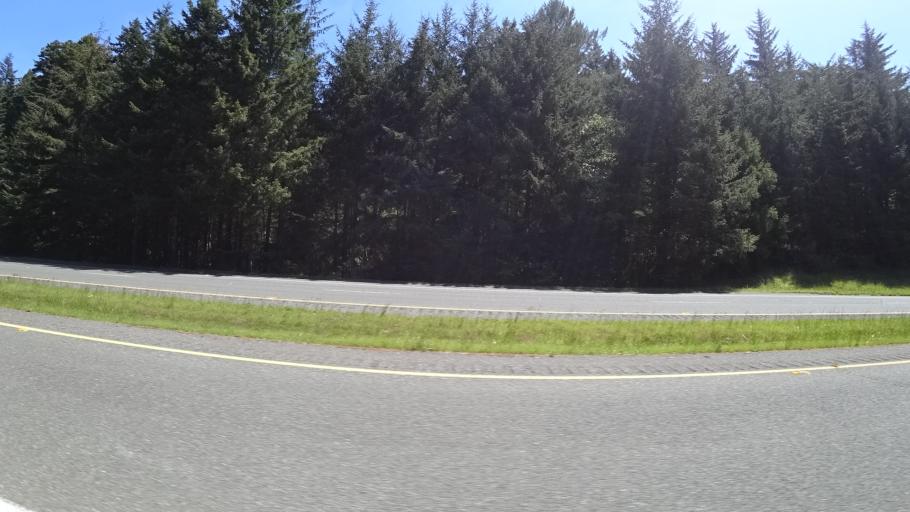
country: US
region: California
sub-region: Humboldt County
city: Westhaven-Moonstone
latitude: 41.1057
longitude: -124.1549
